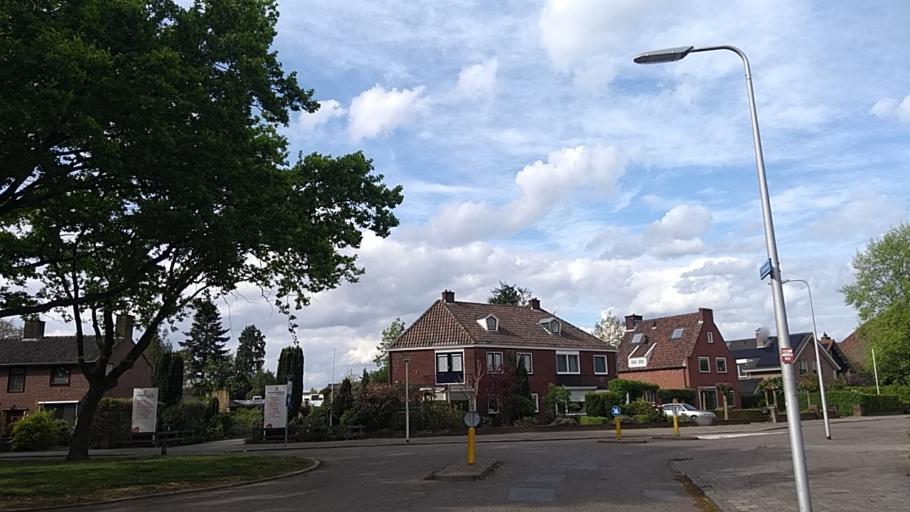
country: NL
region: Overijssel
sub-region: Gemeente Almelo
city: Almelo
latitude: 52.3636
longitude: 6.6625
